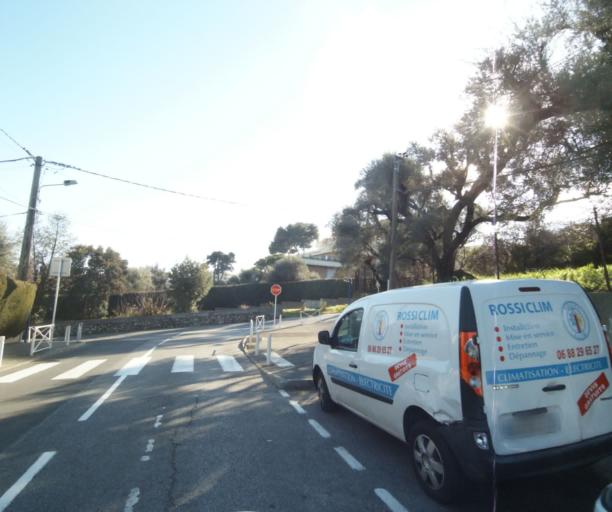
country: FR
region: Provence-Alpes-Cote d'Azur
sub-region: Departement des Alpes-Maritimes
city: Biot
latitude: 43.5969
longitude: 7.1075
